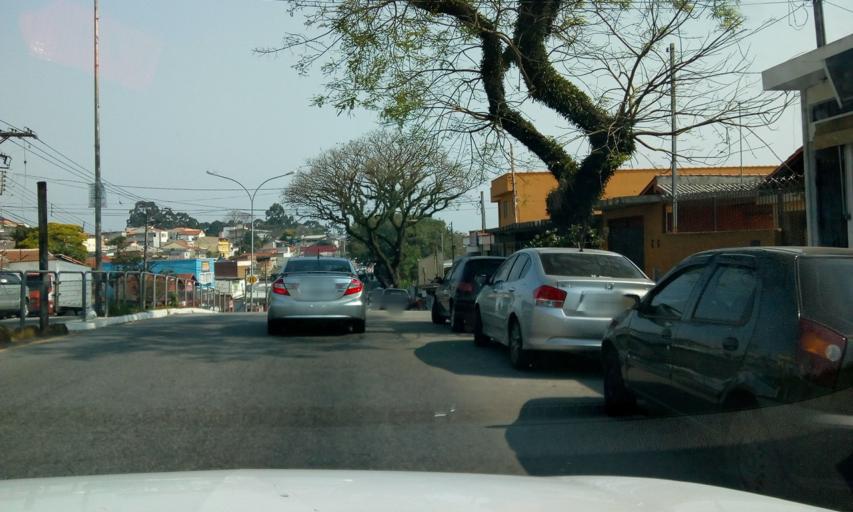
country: BR
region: Sao Paulo
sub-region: Diadema
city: Diadema
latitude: -23.7132
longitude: -46.6895
